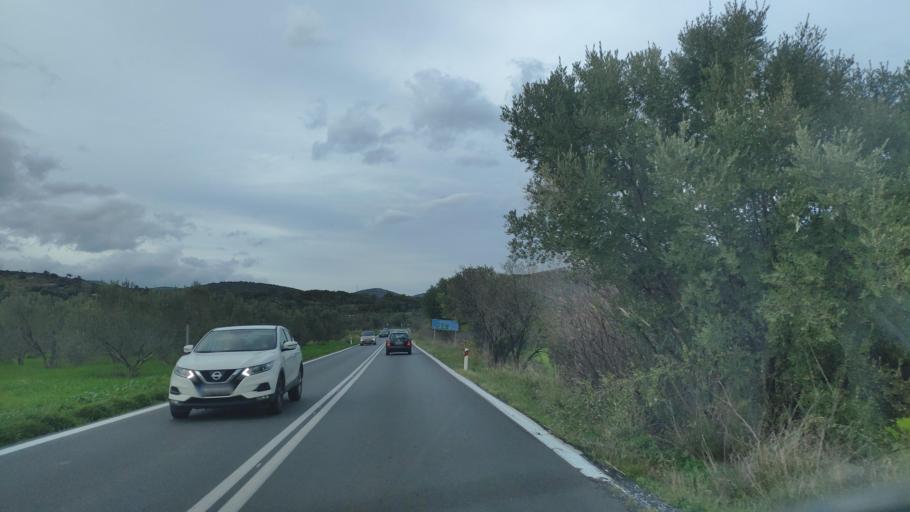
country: GR
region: Peloponnese
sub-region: Nomos Argolidos
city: Koutsopodi
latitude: 37.7580
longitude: 22.7320
